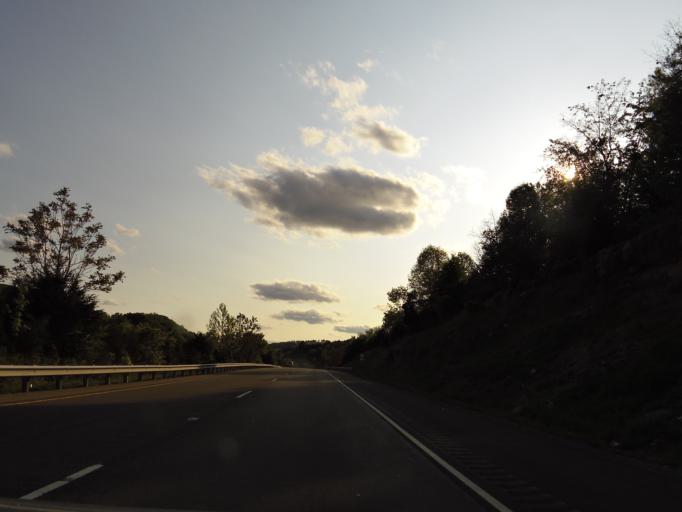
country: US
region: Virginia
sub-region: Tazewell County
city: Raven
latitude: 36.9984
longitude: -81.8259
